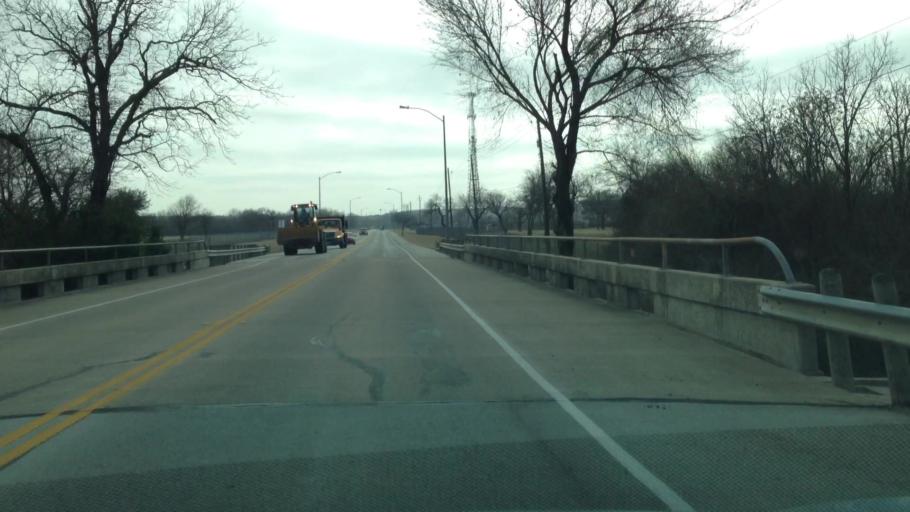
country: US
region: Texas
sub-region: Travis County
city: Hornsby Bend
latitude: 30.1798
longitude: -97.6668
